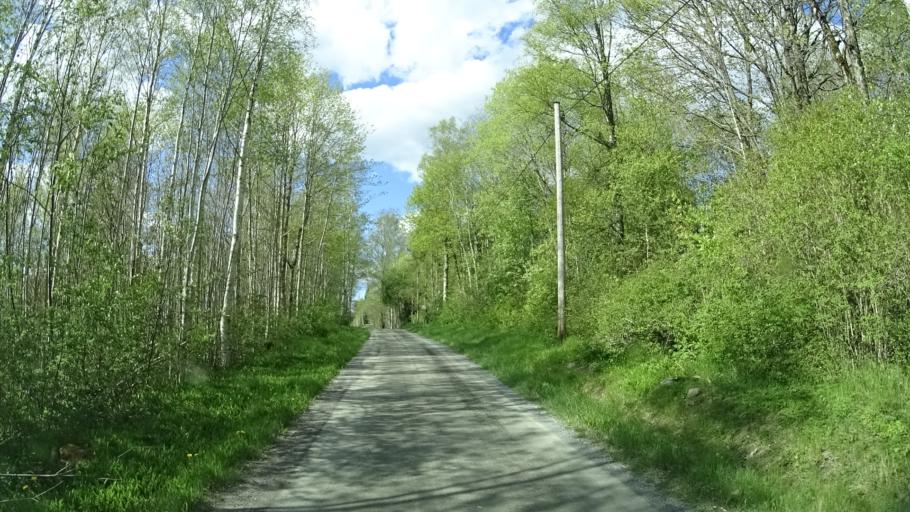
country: SE
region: OErebro
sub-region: Nora Kommun
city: As
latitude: 59.4483
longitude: 14.8096
